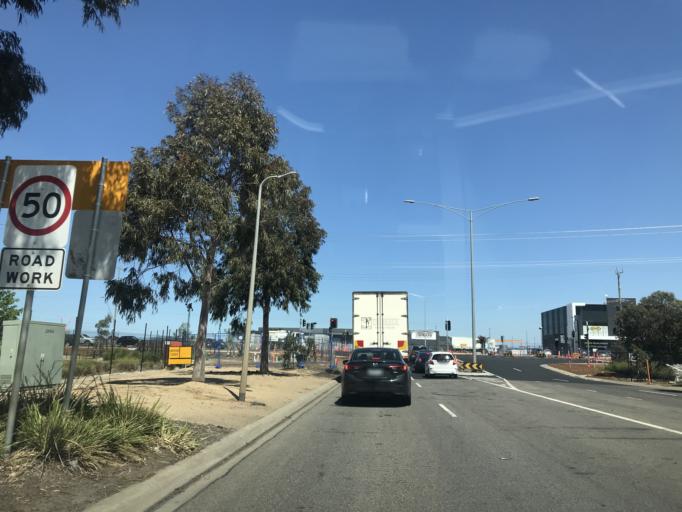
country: AU
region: Victoria
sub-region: Hobsons Bay
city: Laverton
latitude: -37.8412
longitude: 144.7716
